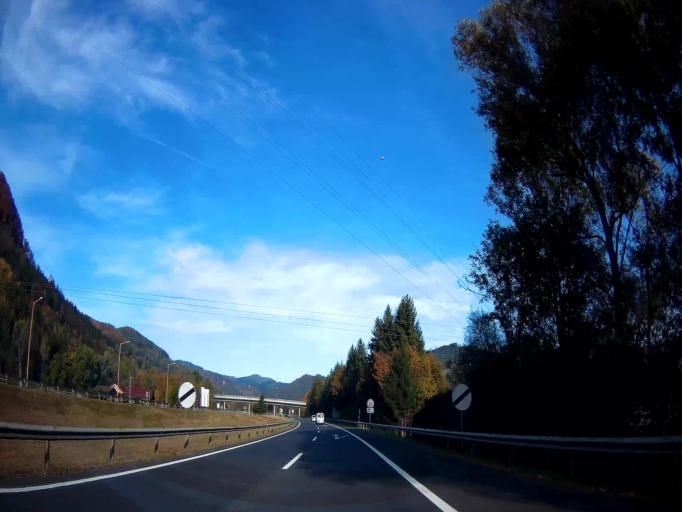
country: AT
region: Styria
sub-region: Politischer Bezirk Graz-Umgebung
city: Deutschfeistritz
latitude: 47.1978
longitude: 15.3253
